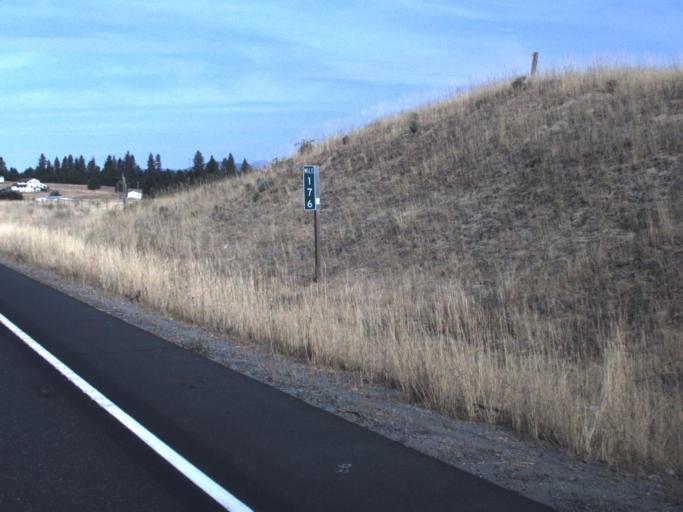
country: US
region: Washington
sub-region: Spokane County
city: Deer Park
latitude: 47.8998
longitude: -117.4361
